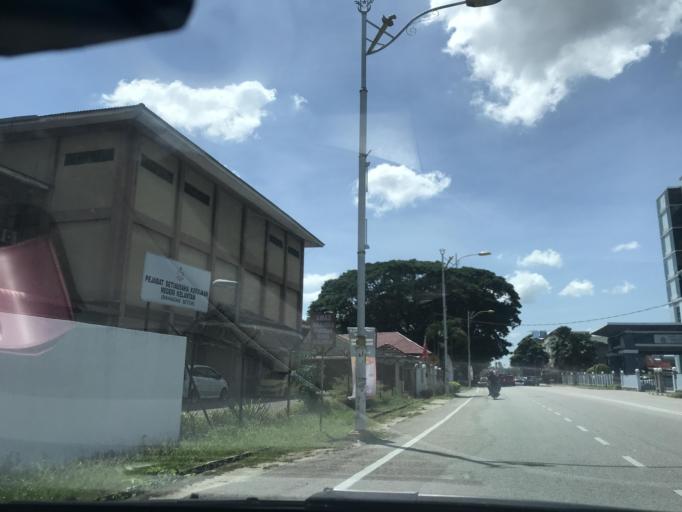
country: MY
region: Kelantan
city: Kota Bharu
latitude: 6.1092
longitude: 102.2383
